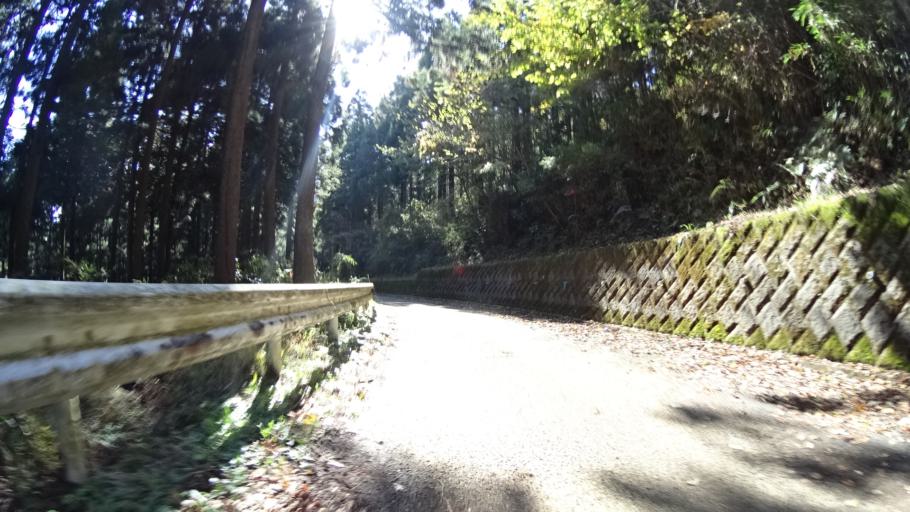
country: JP
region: Kanagawa
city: Zama
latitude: 35.5231
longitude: 139.2748
